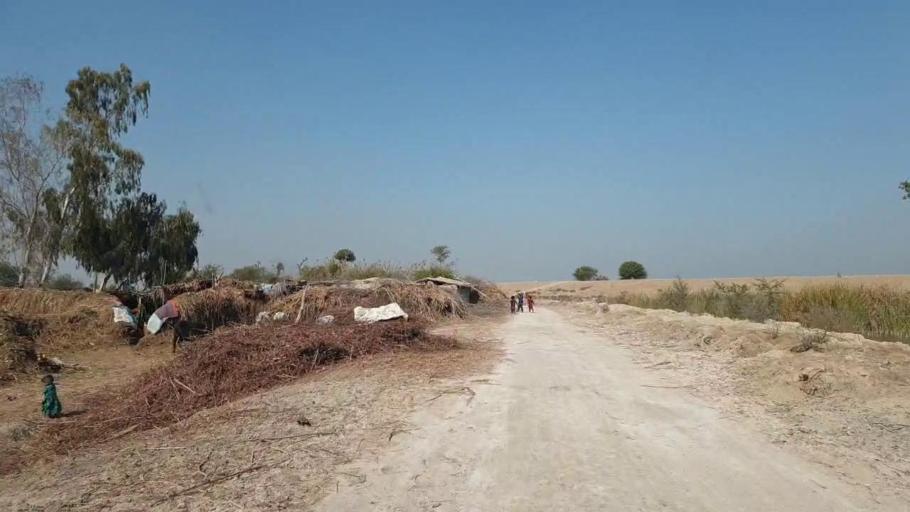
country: PK
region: Sindh
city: Bhit Shah
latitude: 25.9140
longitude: 68.5037
